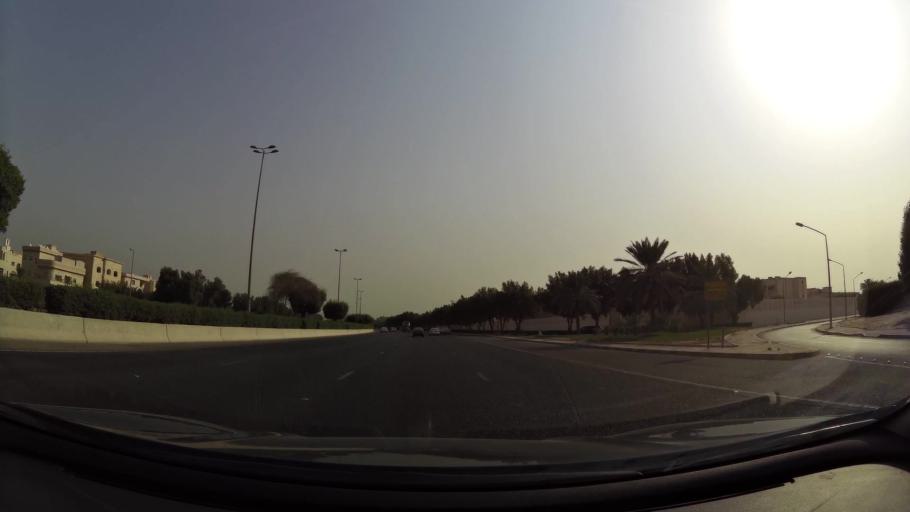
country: KW
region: Mubarak al Kabir
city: Sabah as Salim
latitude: 29.2371
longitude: 48.0713
